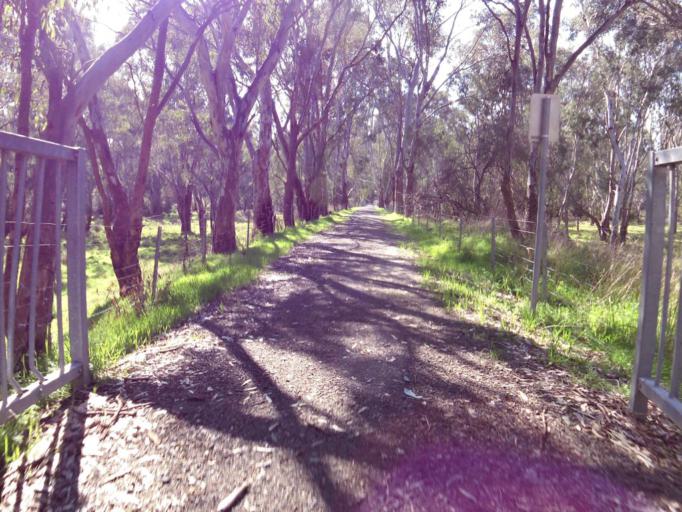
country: AU
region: Victoria
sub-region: Murrindindi
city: Alexandra
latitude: -37.1601
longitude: 145.5644
